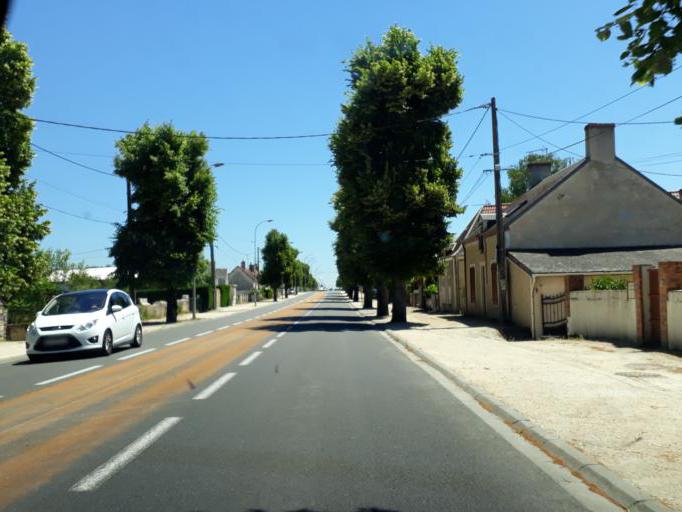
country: FR
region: Centre
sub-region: Departement du Cher
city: Mehun-sur-Yevre
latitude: 47.1431
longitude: 2.2322
